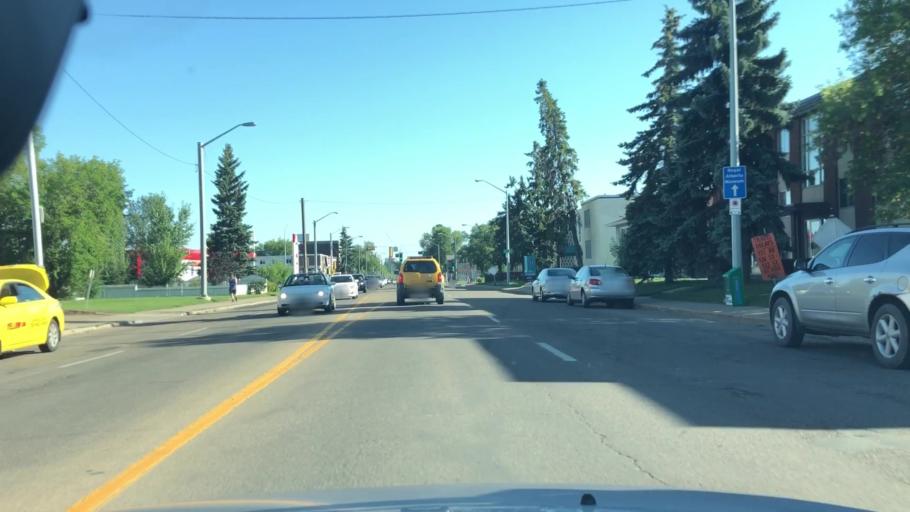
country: CA
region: Alberta
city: Edmonton
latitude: 53.5603
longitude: -113.5360
